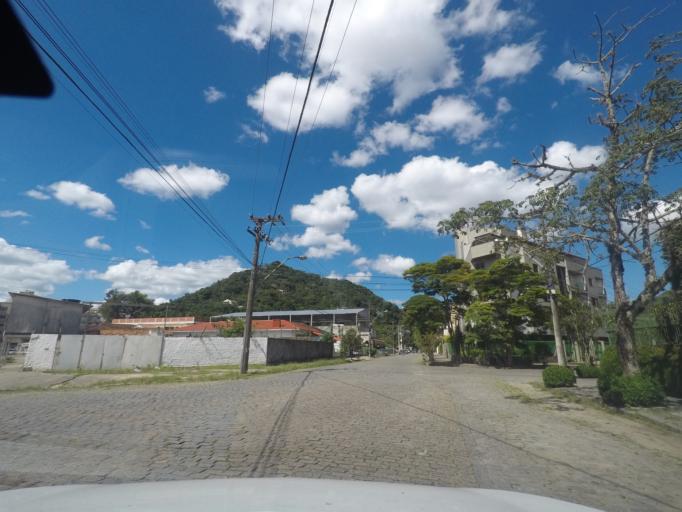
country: BR
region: Rio de Janeiro
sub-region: Teresopolis
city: Teresopolis
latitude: -22.4352
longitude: -42.9762
